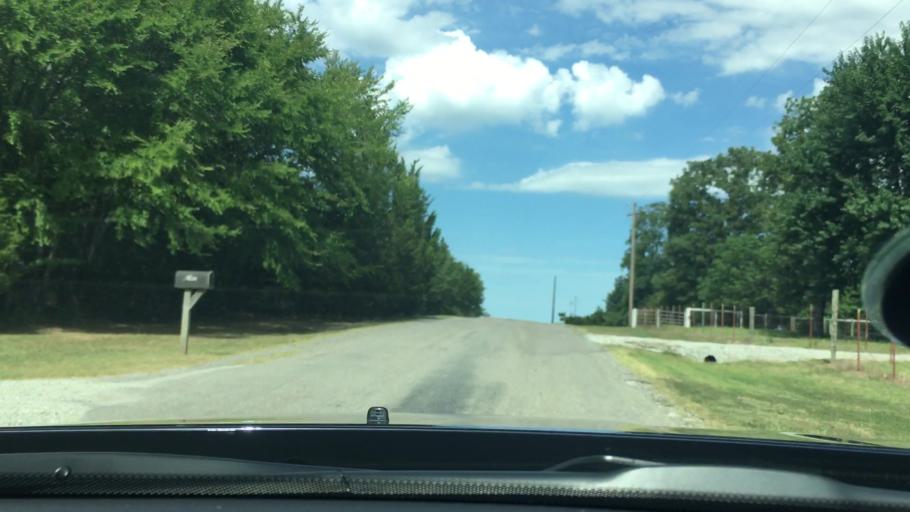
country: US
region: Oklahoma
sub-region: Pontotoc County
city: Ada
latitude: 34.7635
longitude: -96.5803
